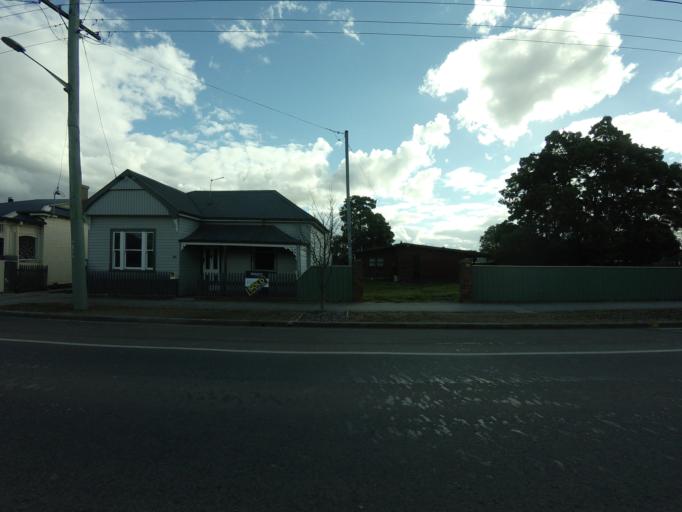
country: AU
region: Tasmania
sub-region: Northern Midlands
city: Longford
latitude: -41.6839
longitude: 147.0808
